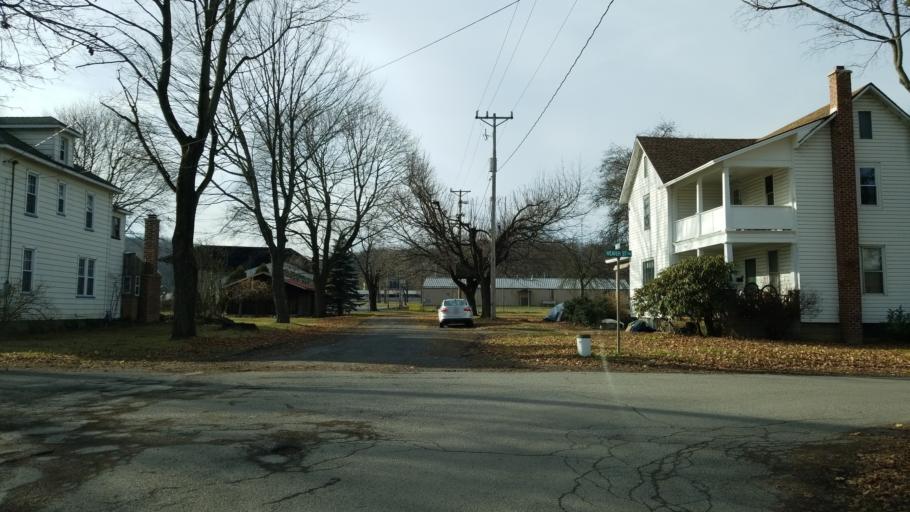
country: US
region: Pennsylvania
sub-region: Clearfield County
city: Clearfield
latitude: 41.0311
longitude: -78.4433
